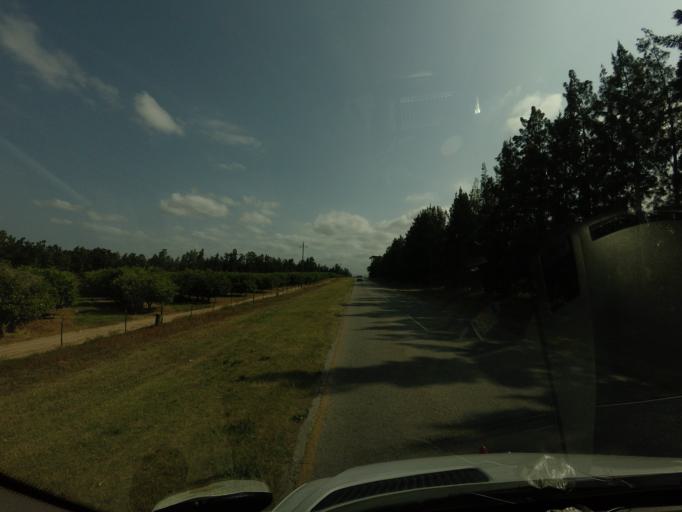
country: ZA
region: Eastern Cape
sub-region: Cacadu District Municipality
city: Kirkwood
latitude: -33.5761
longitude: 25.6787
